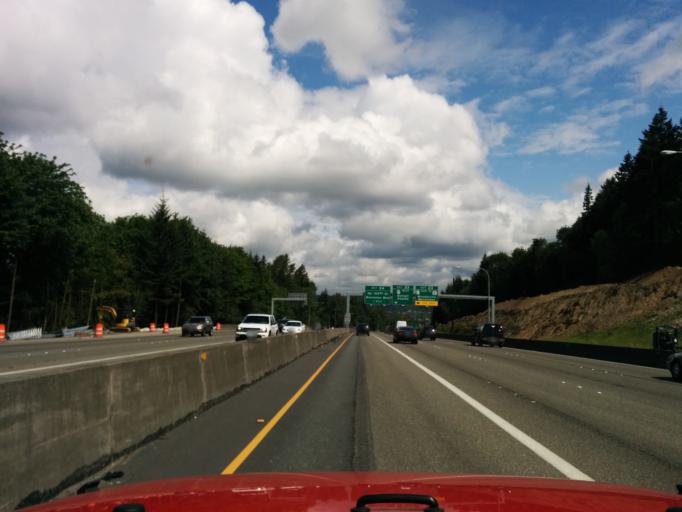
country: US
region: Washington
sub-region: King County
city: Kingsgate
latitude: 47.7480
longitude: -122.1871
